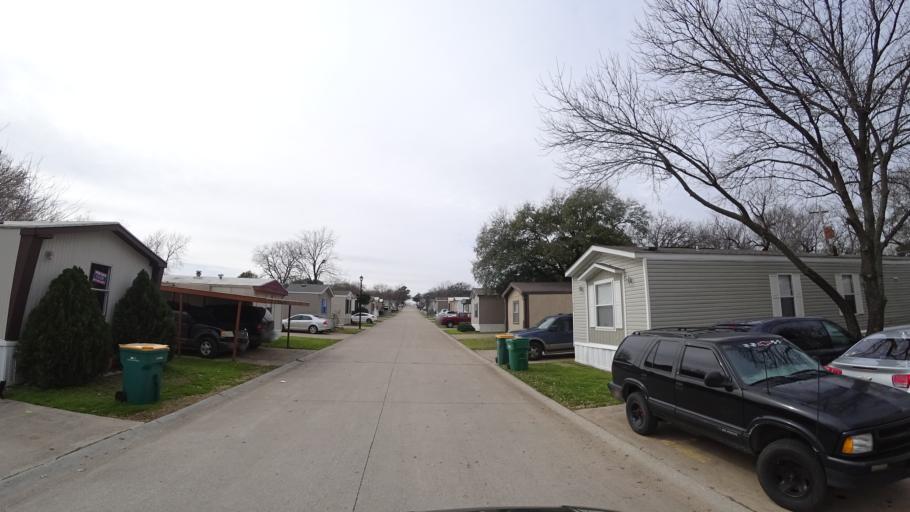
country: US
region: Texas
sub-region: Denton County
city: Lewisville
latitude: 33.0348
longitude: -96.9846
